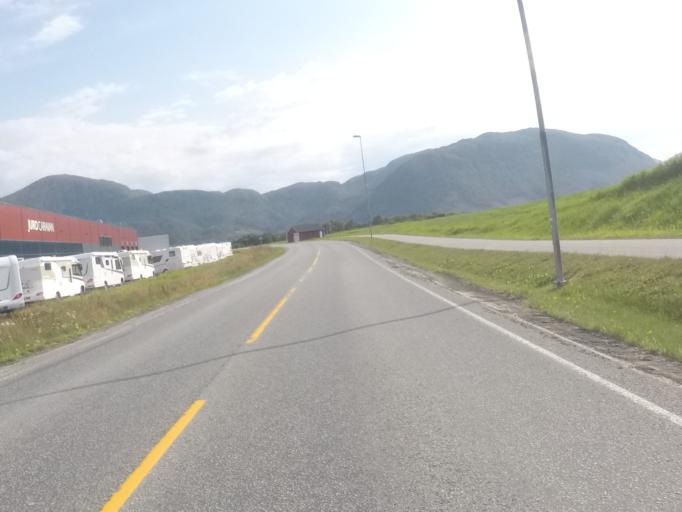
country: NO
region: More og Romsdal
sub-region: Fraena
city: Elnesvagen
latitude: 62.8215
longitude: 7.2376
